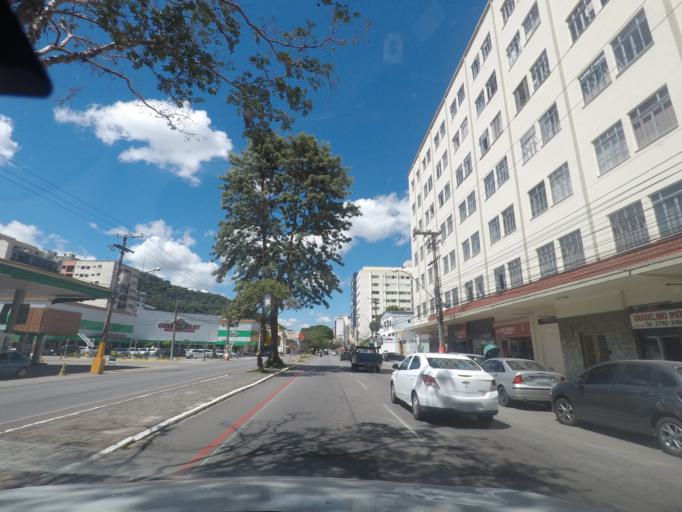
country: BR
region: Rio de Janeiro
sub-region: Teresopolis
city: Teresopolis
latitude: -22.4208
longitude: -42.9755
